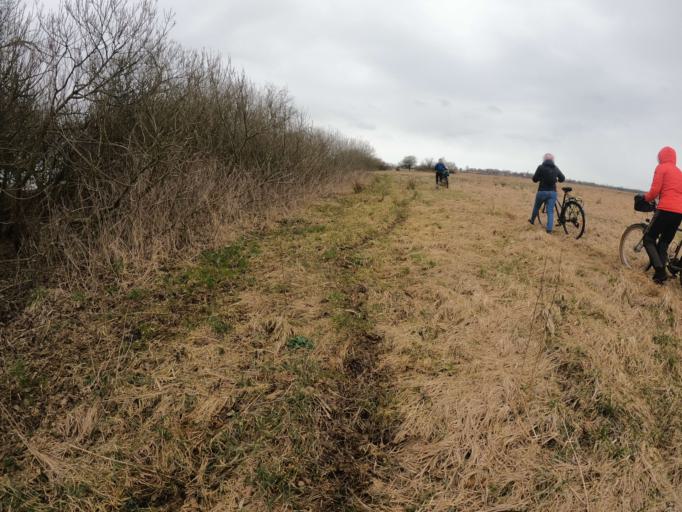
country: PL
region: West Pomeranian Voivodeship
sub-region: Powiat gryficki
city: Trzebiatow
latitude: 54.0762
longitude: 15.2330
